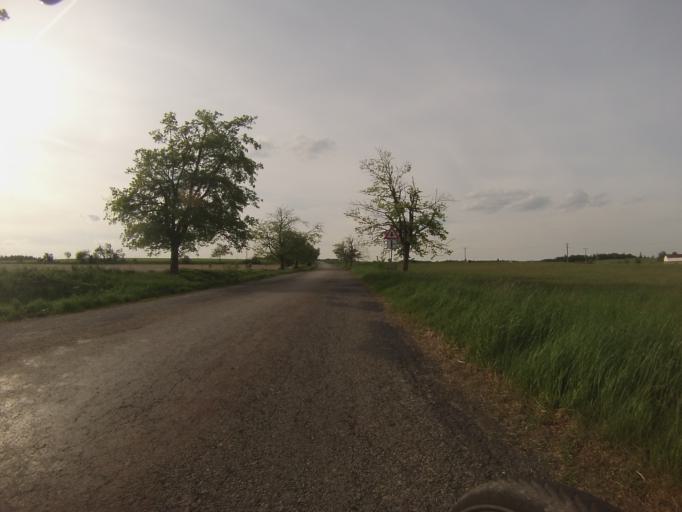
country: CZ
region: Olomoucky
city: Protivanov
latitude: 49.4628
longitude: 16.8688
